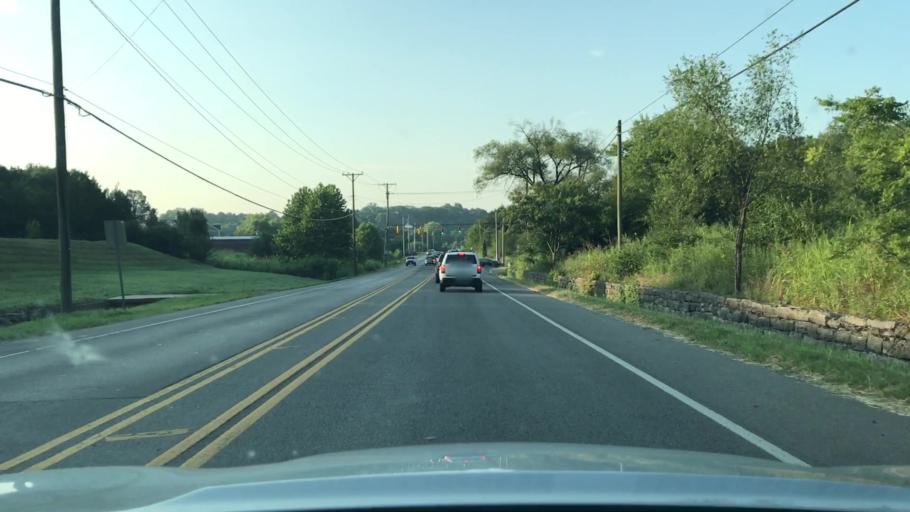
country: US
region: Tennessee
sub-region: Williamson County
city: Nolensville
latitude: 36.0135
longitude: -86.7043
